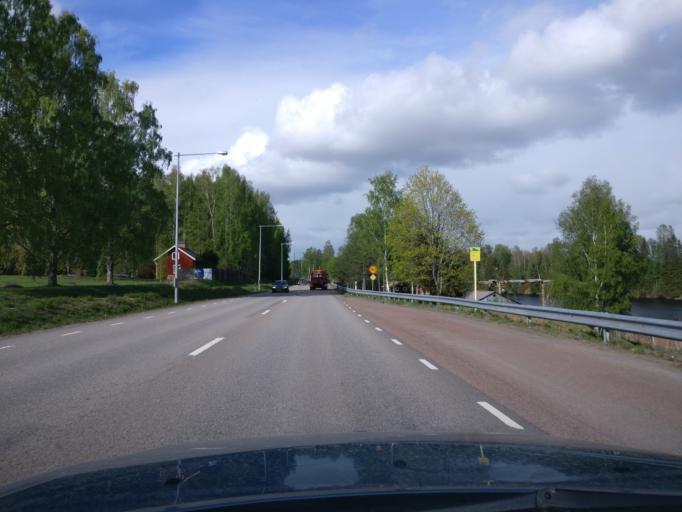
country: SE
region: Vaermland
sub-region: Forshaga Kommun
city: Forshaga
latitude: 59.5170
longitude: 13.4441
